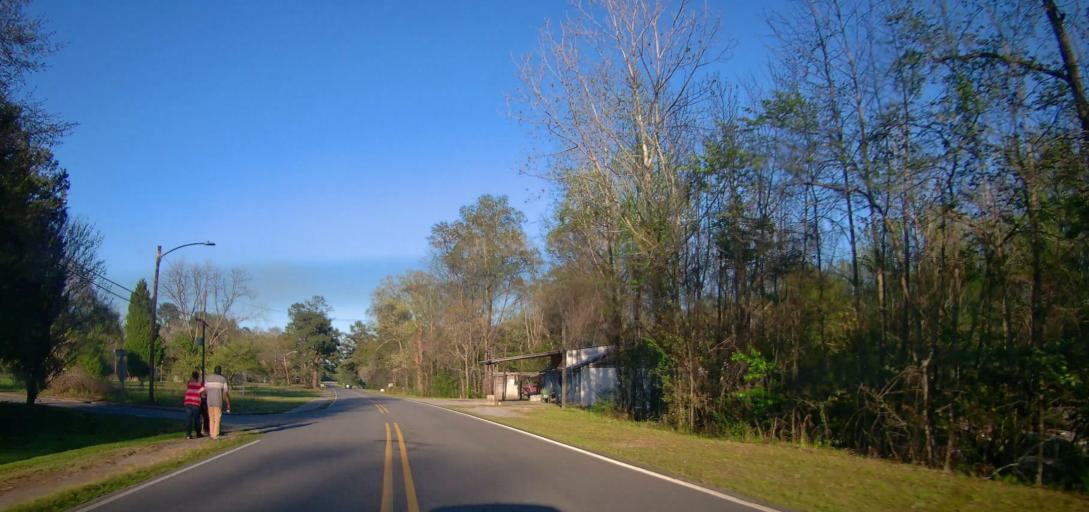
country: US
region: Georgia
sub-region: Wilkinson County
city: Irwinton
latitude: 32.8463
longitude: -83.2037
